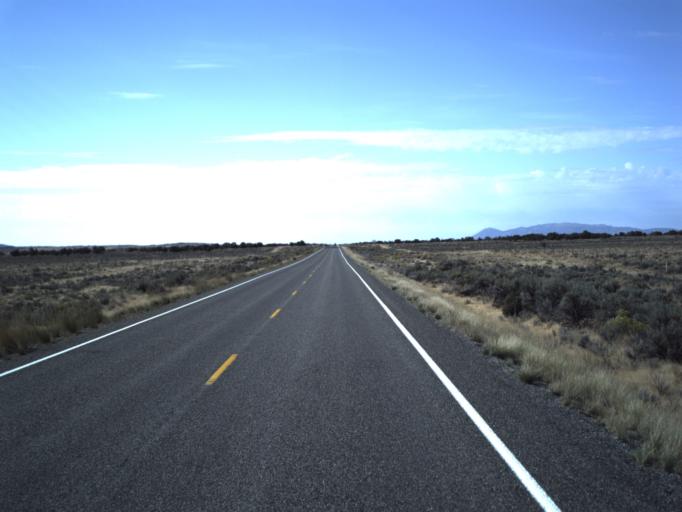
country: US
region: Idaho
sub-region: Cassia County
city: Burley
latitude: 41.7251
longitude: -113.5250
